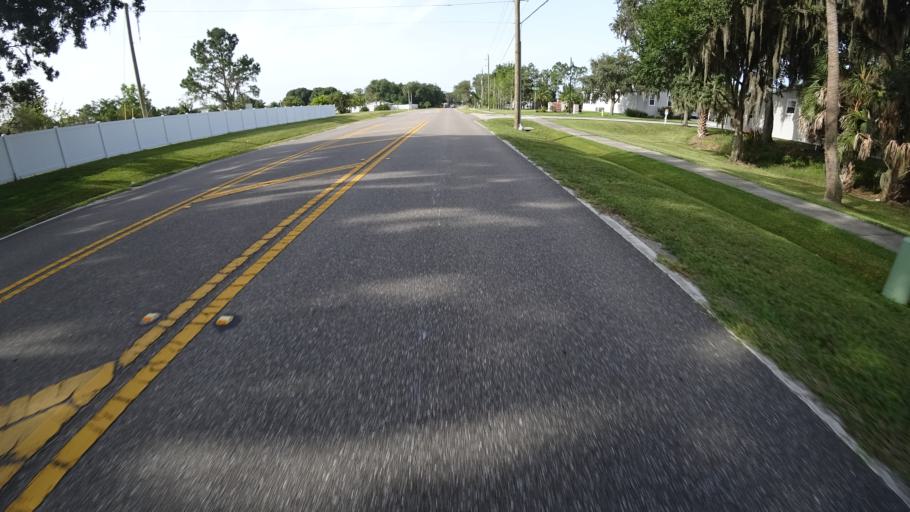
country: US
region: Florida
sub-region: Manatee County
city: Ellenton
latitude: 27.5444
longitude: -82.4911
